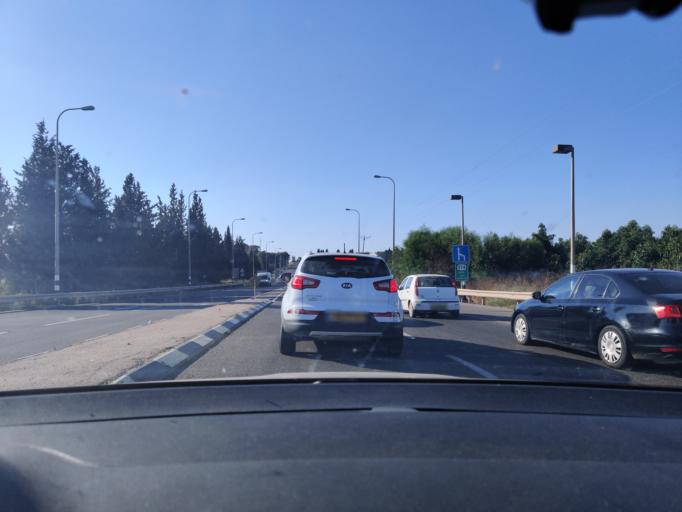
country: PS
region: West Bank
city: Nazlat `Isa
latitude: 32.4446
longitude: 35.0217
